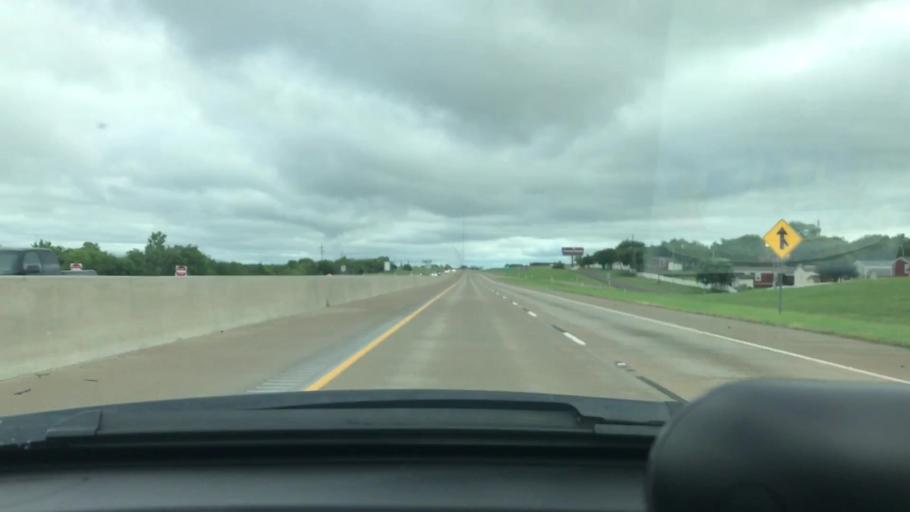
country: US
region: Texas
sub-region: Grayson County
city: Howe
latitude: 33.5116
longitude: -96.6169
